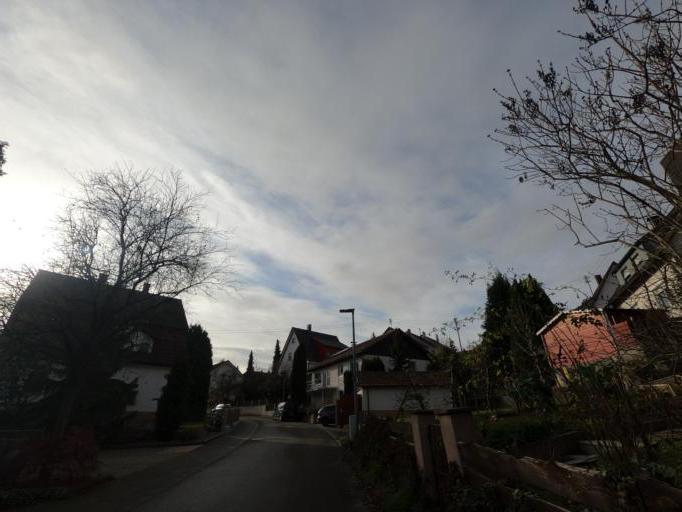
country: DE
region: Baden-Wuerttemberg
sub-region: Regierungsbezirk Stuttgart
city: Albershausen
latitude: 48.6989
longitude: 9.5690
